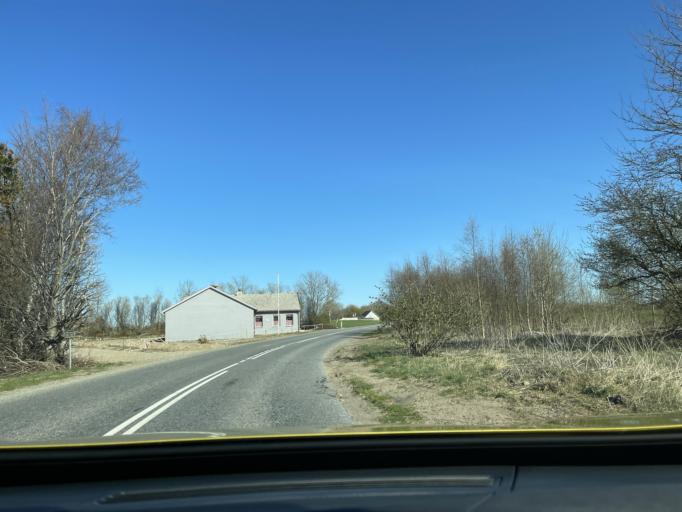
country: DK
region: Central Jutland
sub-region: Silkeborg Kommune
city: Kjellerup
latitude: 56.2568
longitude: 9.3586
